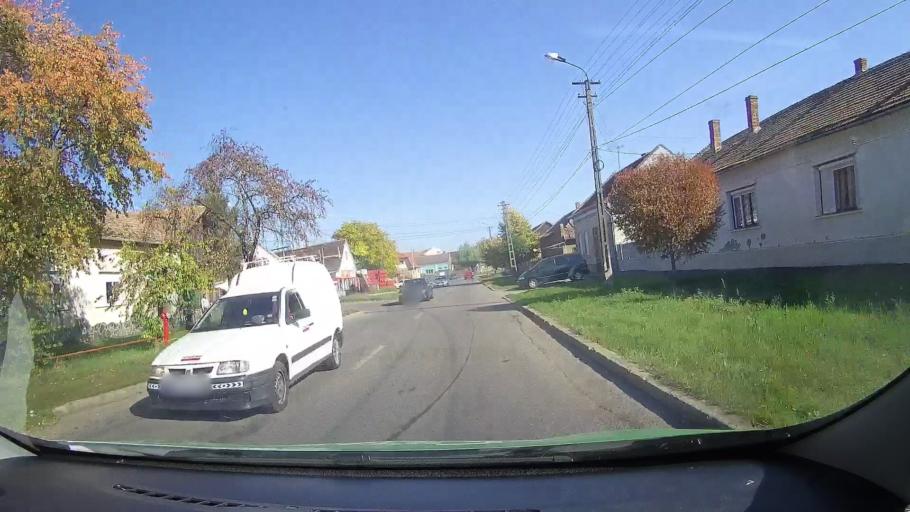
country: RO
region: Satu Mare
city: Carei
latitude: 47.6783
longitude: 22.4711
